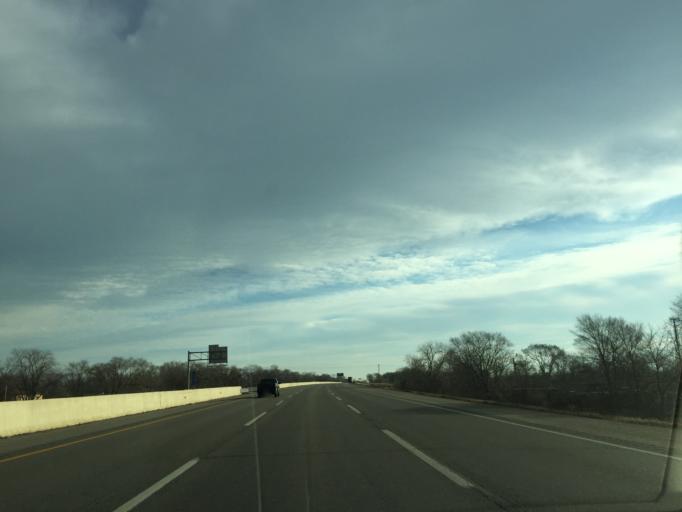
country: US
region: Indiana
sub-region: Lake County
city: New Chicago
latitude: 41.5879
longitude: -87.2834
